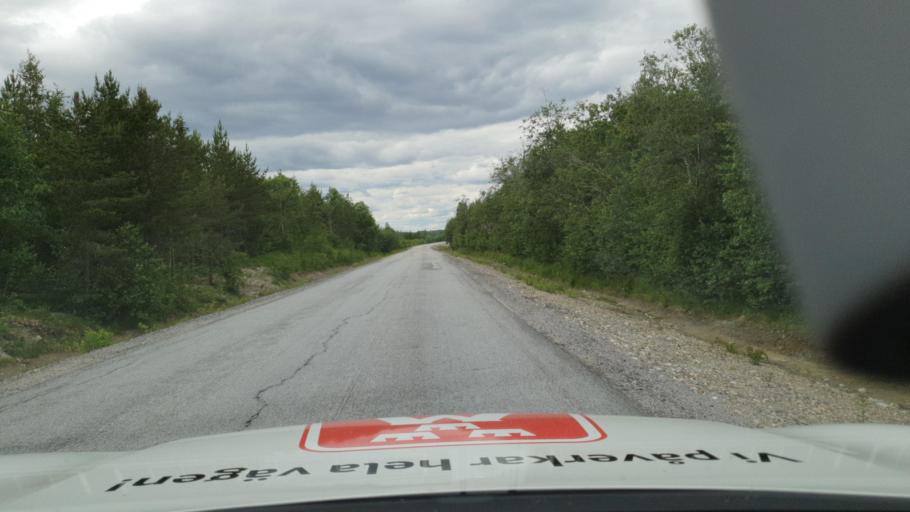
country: SE
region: Vaesterbotten
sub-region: Bjurholms Kommun
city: Bjurholm
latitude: 63.7689
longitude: 19.2541
